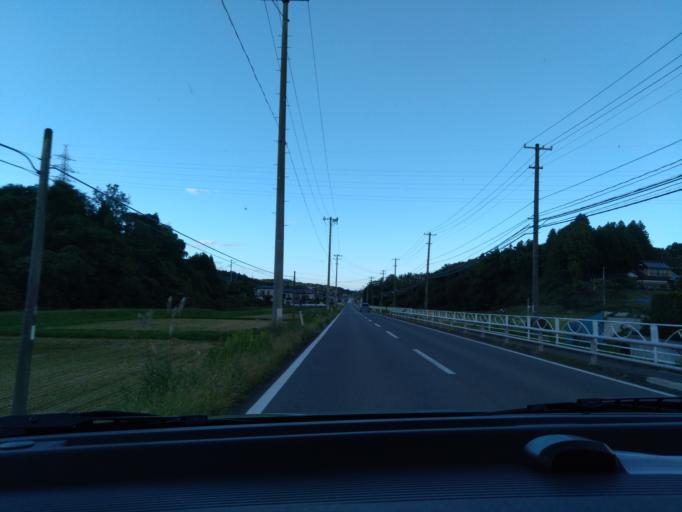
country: JP
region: Iwate
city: Ichinoseki
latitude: 38.8926
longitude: 141.1318
